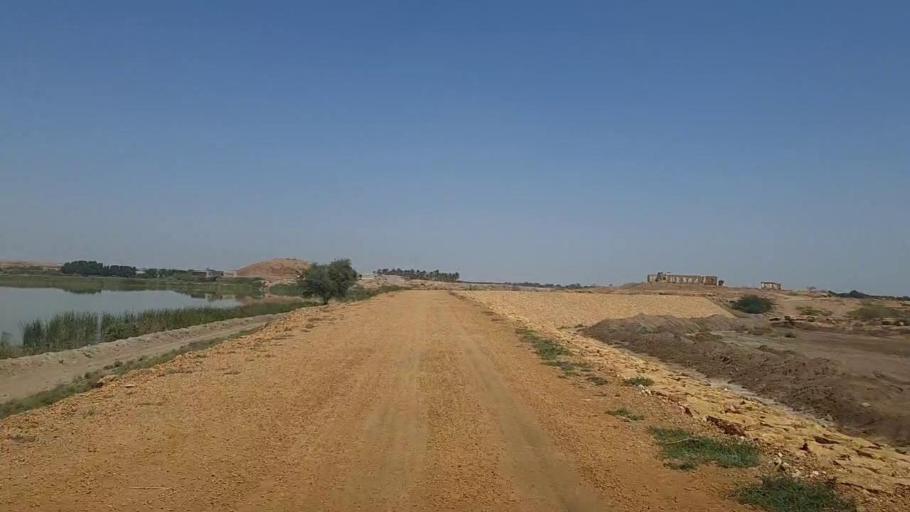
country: PK
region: Sindh
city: Thatta
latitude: 24.8062
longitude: 68.0032
